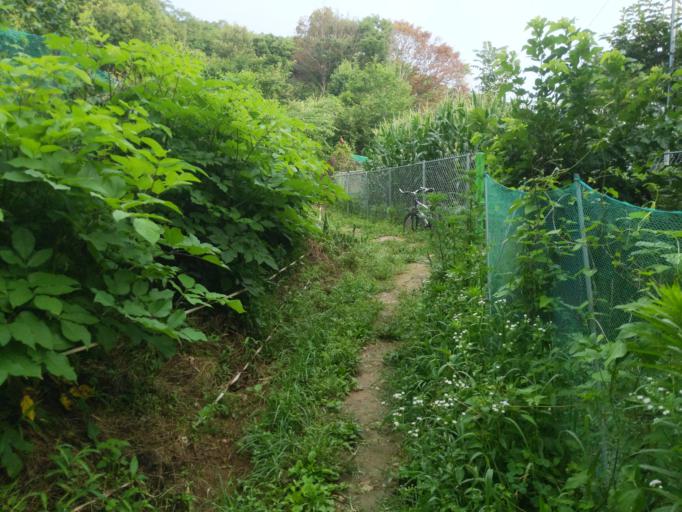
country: KR
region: Daegu
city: Hwawon
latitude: 35.8018
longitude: 128.5266
